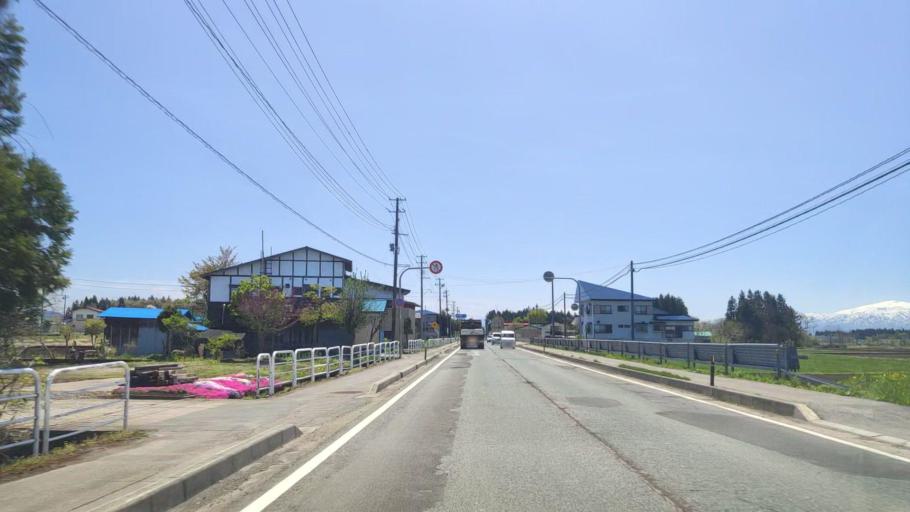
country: JP
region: Yamagata
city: Shinjo
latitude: 38.8285
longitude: 140.3278
